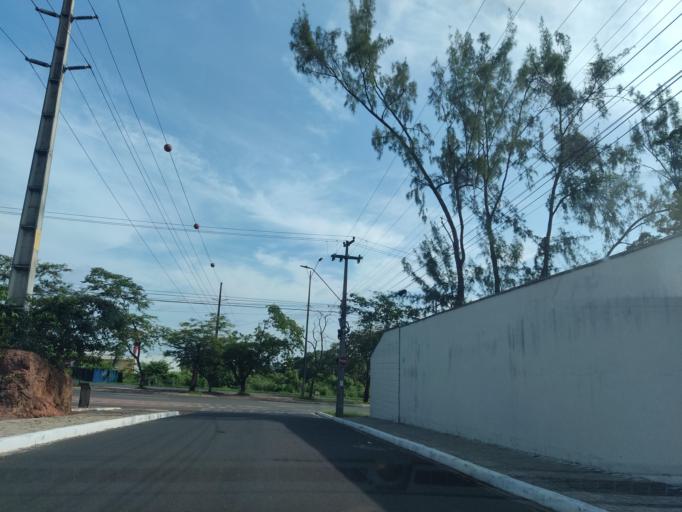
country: BR
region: Piaui
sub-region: Teresina
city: Teresina
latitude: -5.0782
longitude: -42.7516
